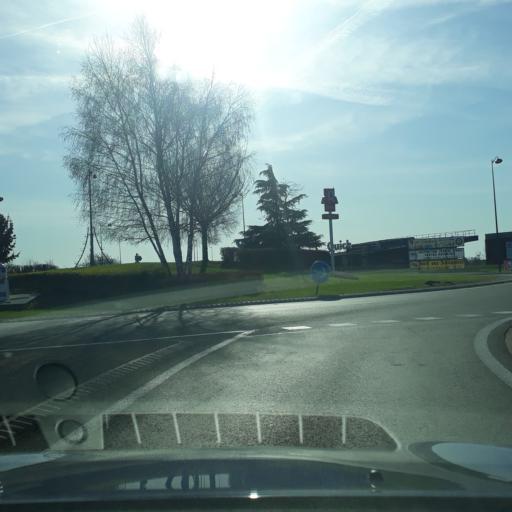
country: FR
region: Ile-de-France
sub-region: Departement de l'Essonne
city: Etampes
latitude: 48.4419
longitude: 2.1362
